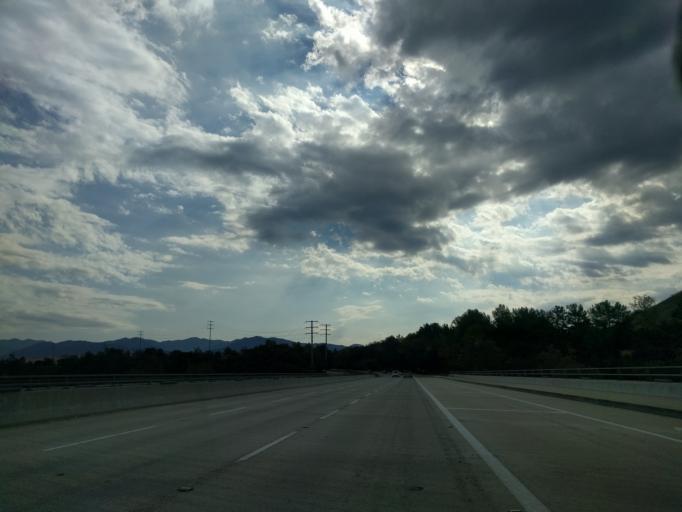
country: US
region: California
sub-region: Orange County
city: Rancho Santa Margarita
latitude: 33.6377
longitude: -117.6154
